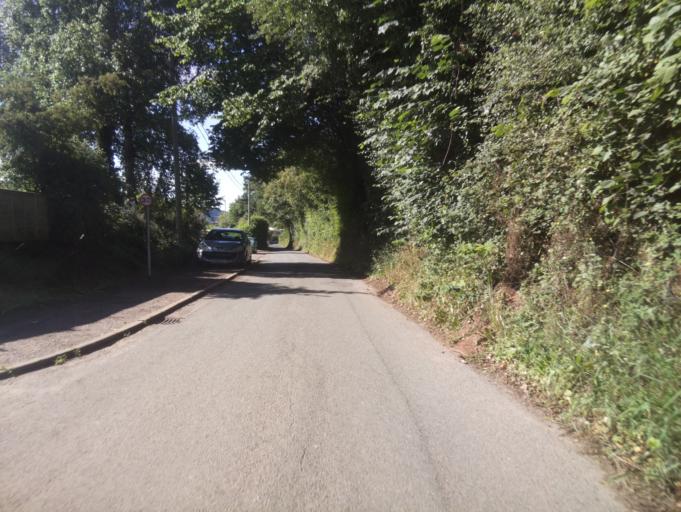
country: GB
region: England
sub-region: Herefordshire
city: Ross on Wye
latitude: 51.9352
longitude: -2.5781
